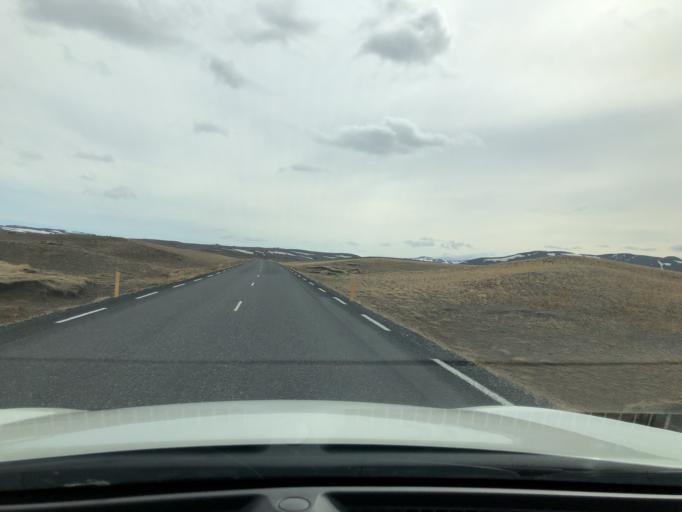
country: IS
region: Northeast
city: Laugar
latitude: 65.5912
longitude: -16.1103
